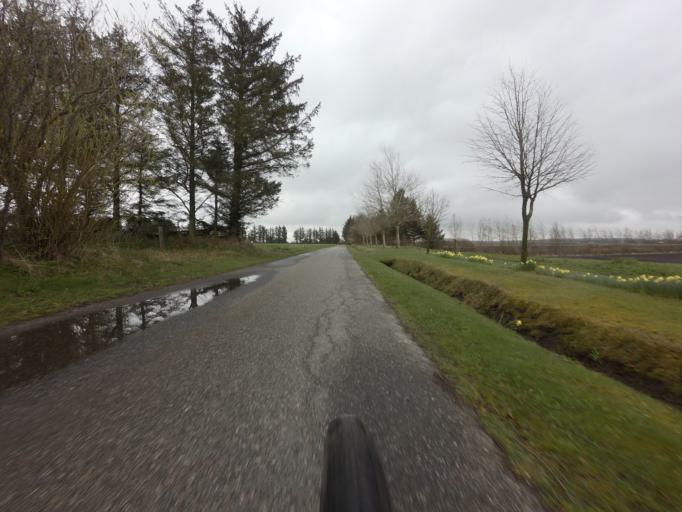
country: DK
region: North Denmark
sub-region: Jammerbugt Kommune
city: Pandrup
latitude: 57.3222
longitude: 9.7942
